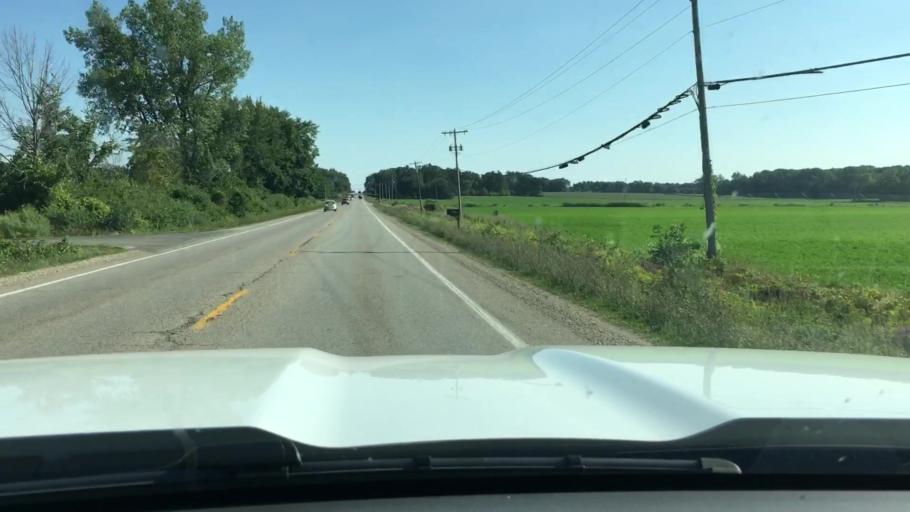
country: US
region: Michigan
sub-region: Ottawa County
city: Allendale
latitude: 43.0043
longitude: -85.9552
